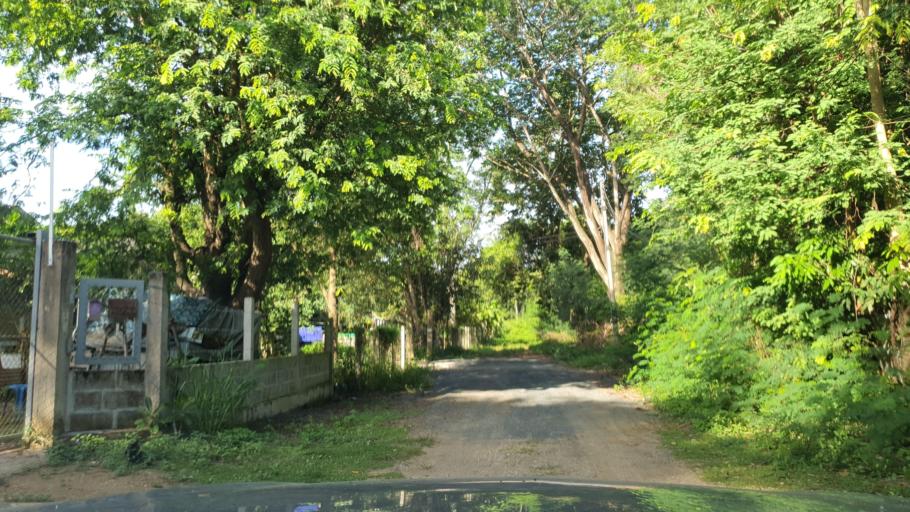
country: TH
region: Chiang Mai
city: San Kamphaeng
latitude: 18.7496
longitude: 99.1019
